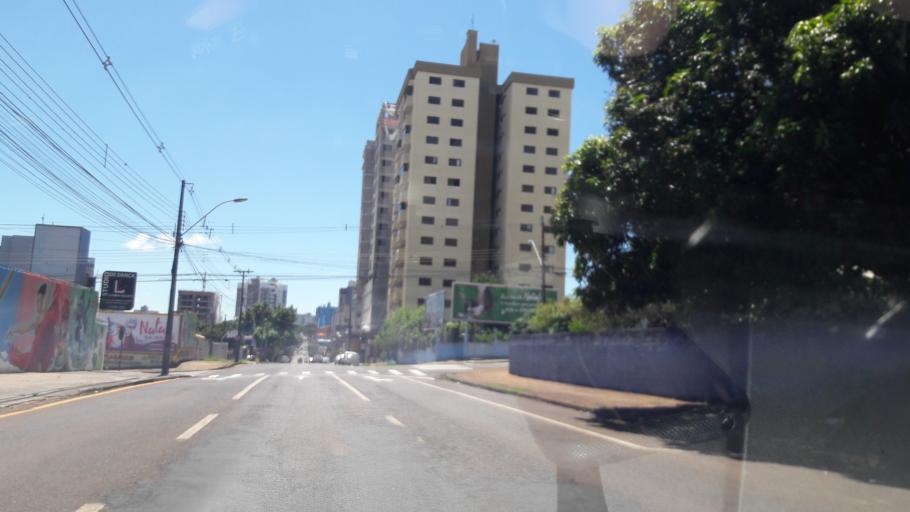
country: BR
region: Parana
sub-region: Cascavel
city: Cascavel
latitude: -24.9513
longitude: -53.4730
